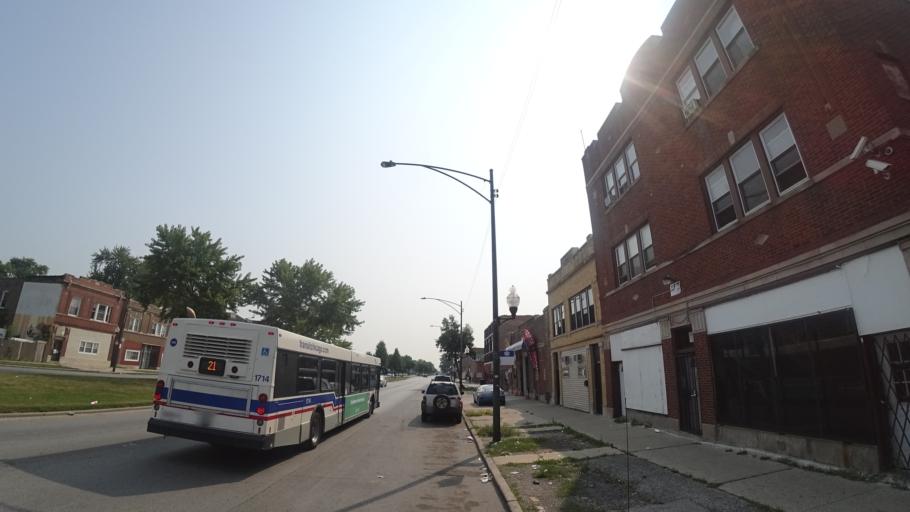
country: US
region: Illinois
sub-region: Cook County
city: Cicero
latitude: 41.8513
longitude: -87.7322
